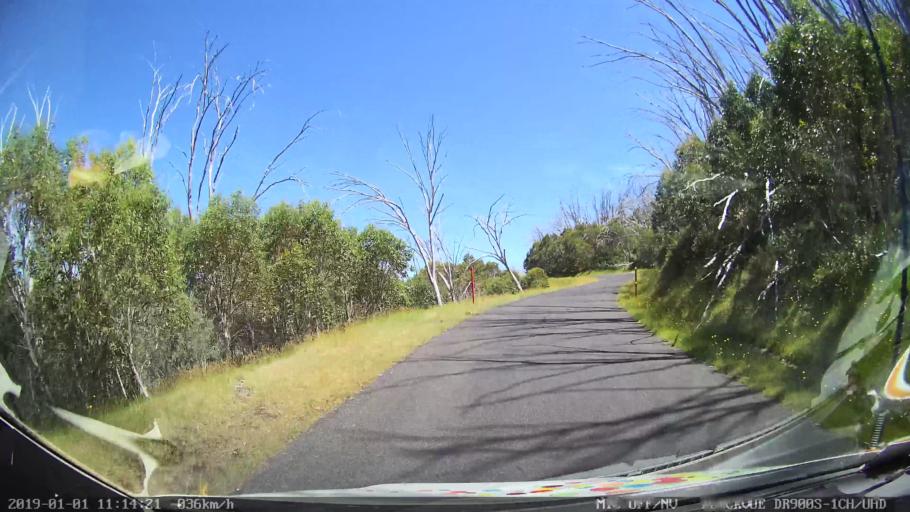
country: AU
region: New South Wales
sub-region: Snowy River
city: Jindabyne
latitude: -35.9513
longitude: 148.3892
